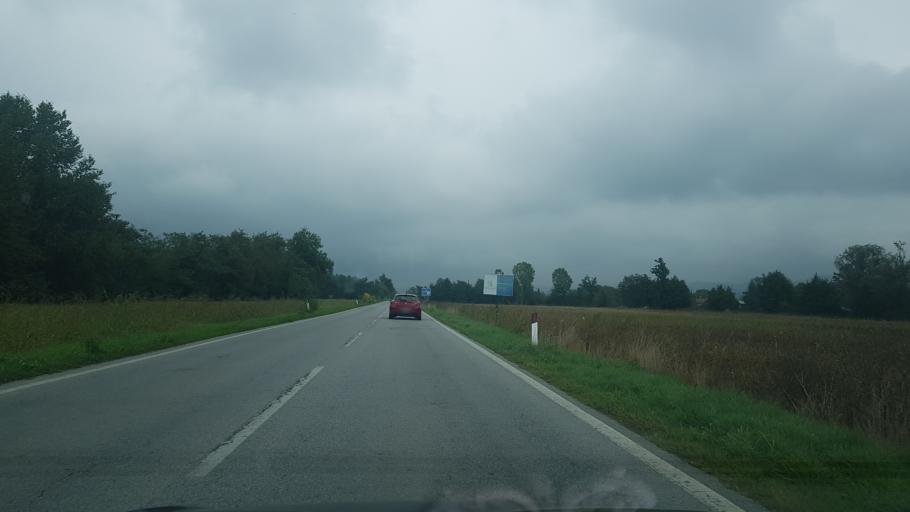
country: IT
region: Piedmont
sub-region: Provincia di Cuneo
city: Briaglia
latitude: 44.4294
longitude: 7.8588
